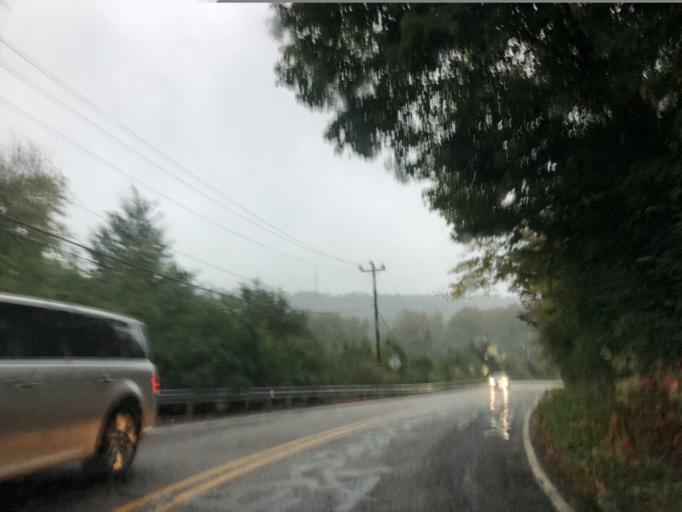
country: US
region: Ohio
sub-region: Hamilton County
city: The Village of Indian Hill
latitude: 39.2494
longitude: -84.2985
